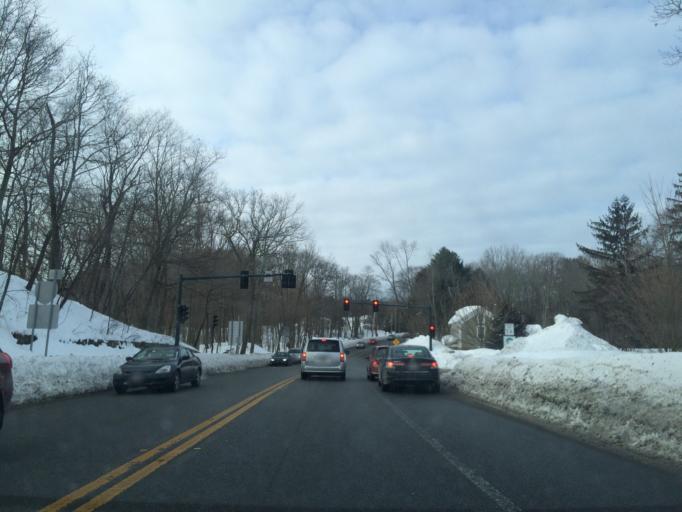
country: US
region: Massachusetts
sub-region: Middlesex County
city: Weston
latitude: 42.3685
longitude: -71.2728
